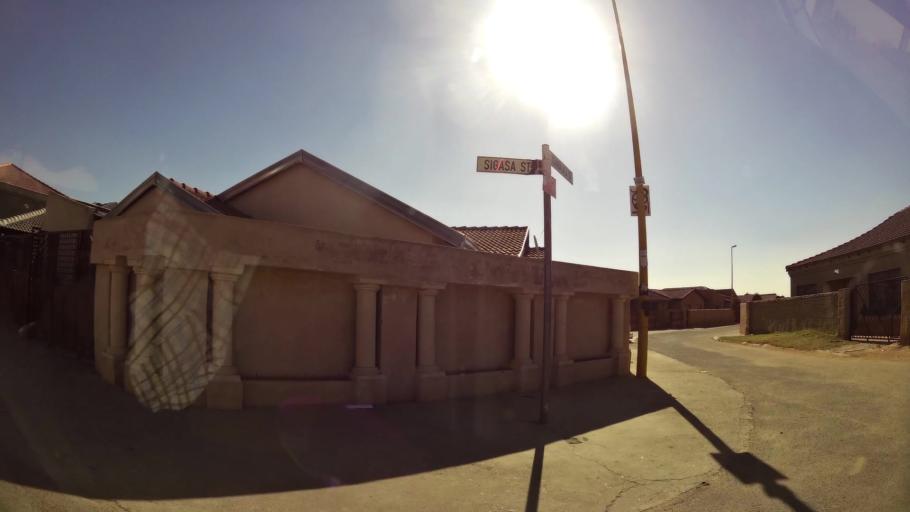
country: ZA
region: Gauteng
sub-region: Ekurhuleni Metropolitan Municipality
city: Tembisa
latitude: -26.0219
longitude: 28.2306
